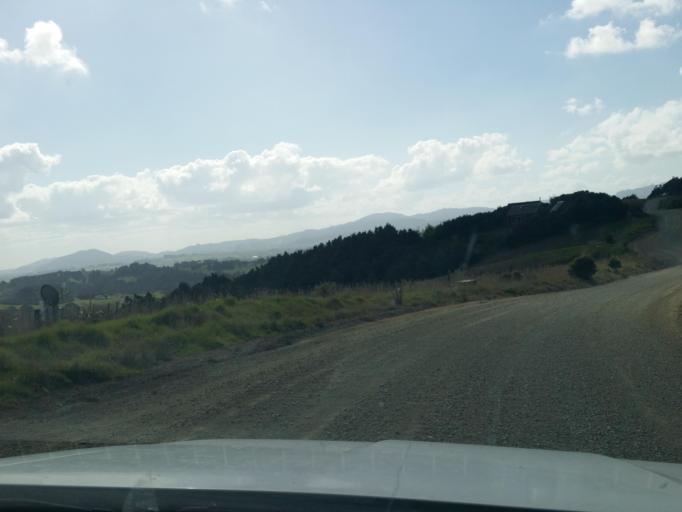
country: NZ
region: Auckland
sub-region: Auckland
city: Wellsford
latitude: -36.1712
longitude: 174.5558
